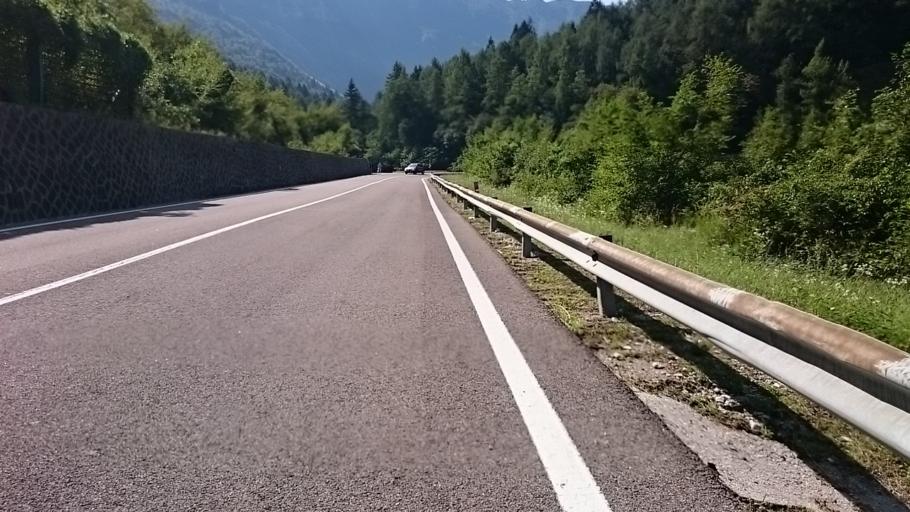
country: IT
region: Veneto
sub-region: Provincia di Belluno
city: Farra d'Alpago
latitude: 46.0902
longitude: 12.3427
